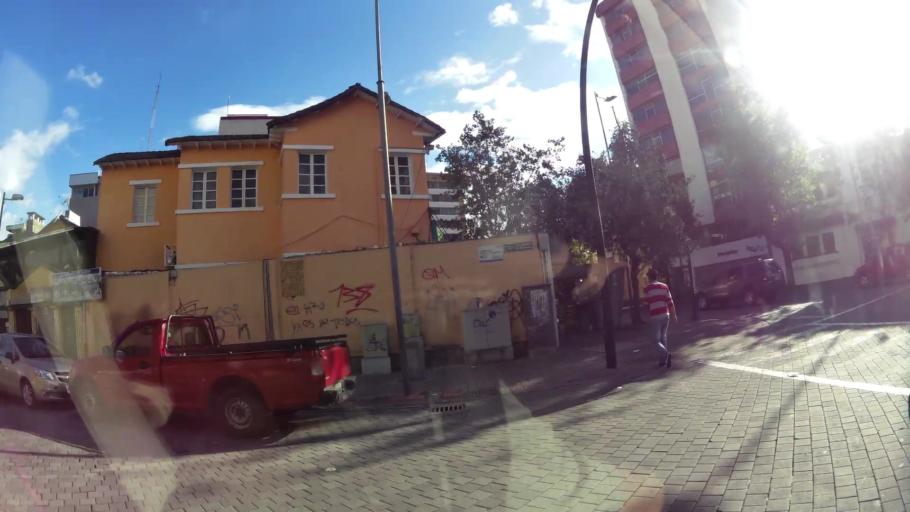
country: EC
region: Pichincha
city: Quito
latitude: -0.2027
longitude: -78.4940
